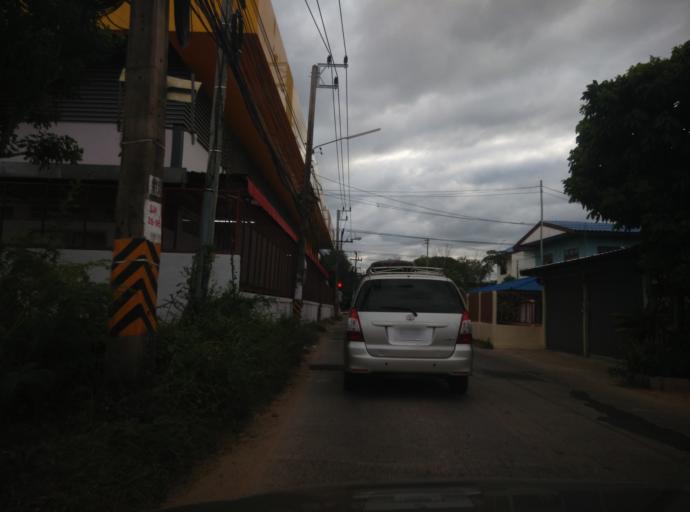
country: TH
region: Sisaket
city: Si Sa Ket
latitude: 15.1117
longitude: 104.3538
